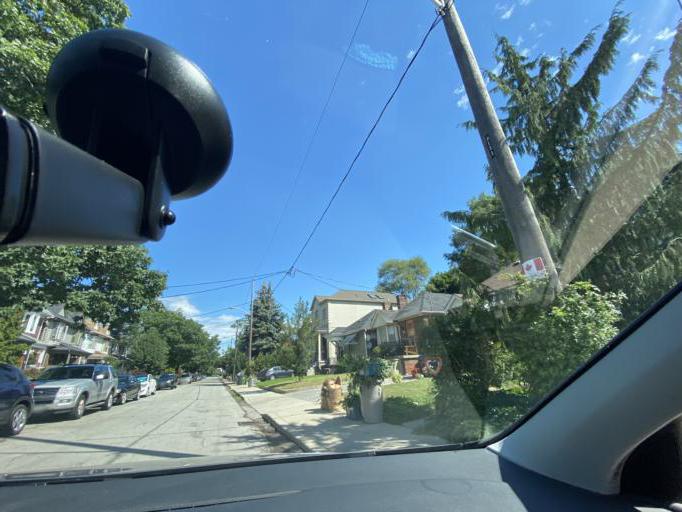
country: CA
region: Ontario
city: Etobicoke
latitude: 43.6638
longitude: -79.4931
